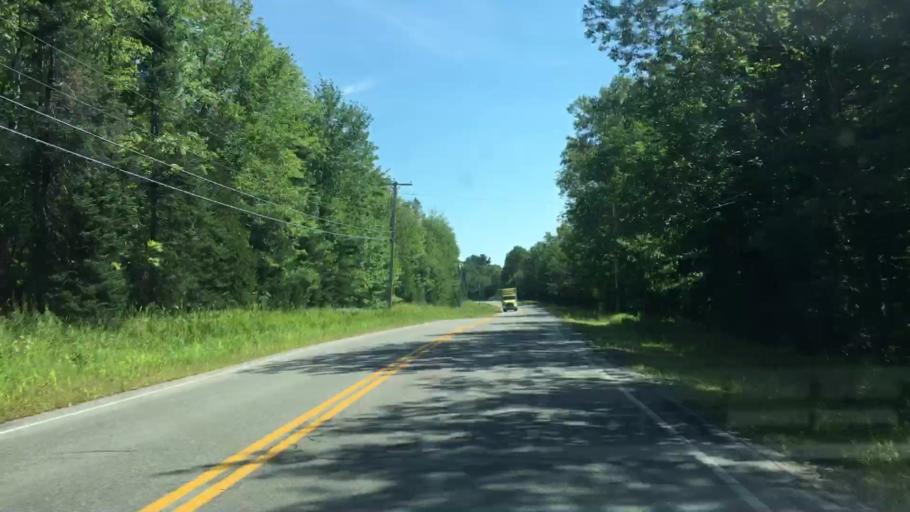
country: US
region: Maine
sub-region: Piscataquis County
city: Milo
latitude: 45.1968
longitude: -68.9037
